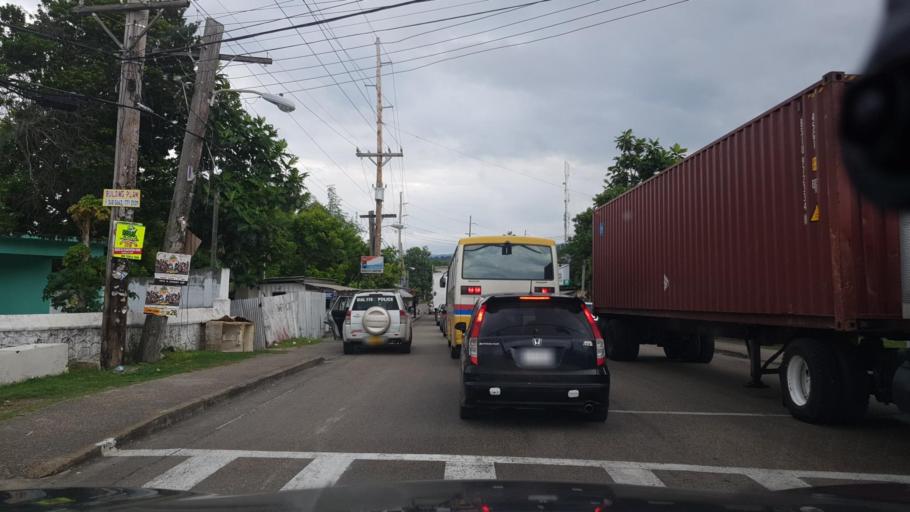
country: JM
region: Saint Ann
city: Saint Ann's Bay
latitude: 18.4465
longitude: -77.2238
